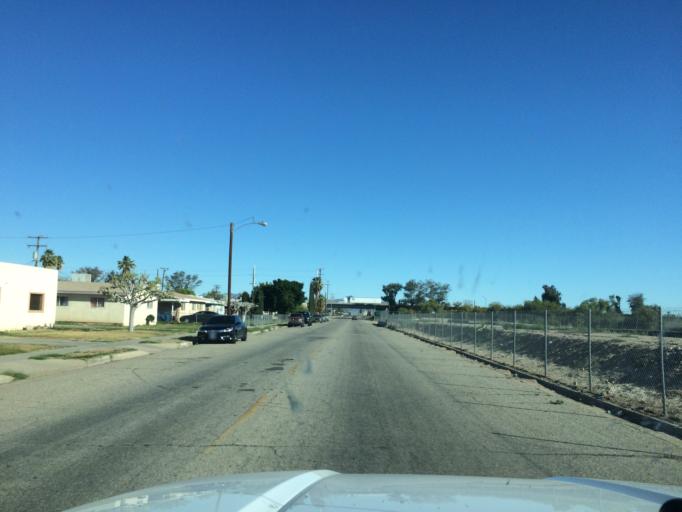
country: US
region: California
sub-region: Riverside County
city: Blythe
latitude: 33.6046
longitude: -114.5880
